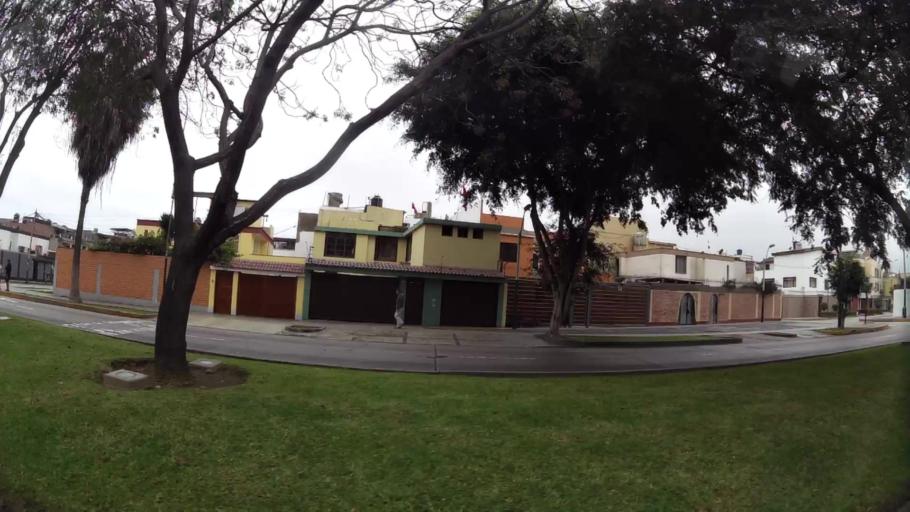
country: PE
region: Lima
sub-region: Lima
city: Surco
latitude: -12.1412
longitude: -77.0013
